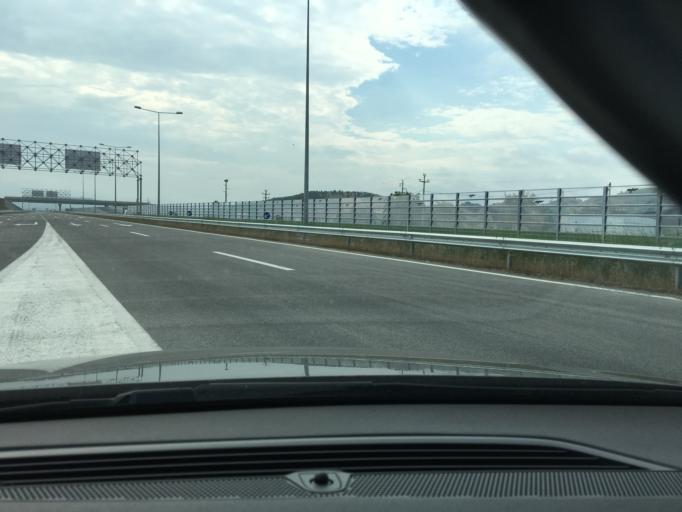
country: MK
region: Sveti Nikole
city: Sveti Nikole
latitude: 41.8113
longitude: 22.0432
